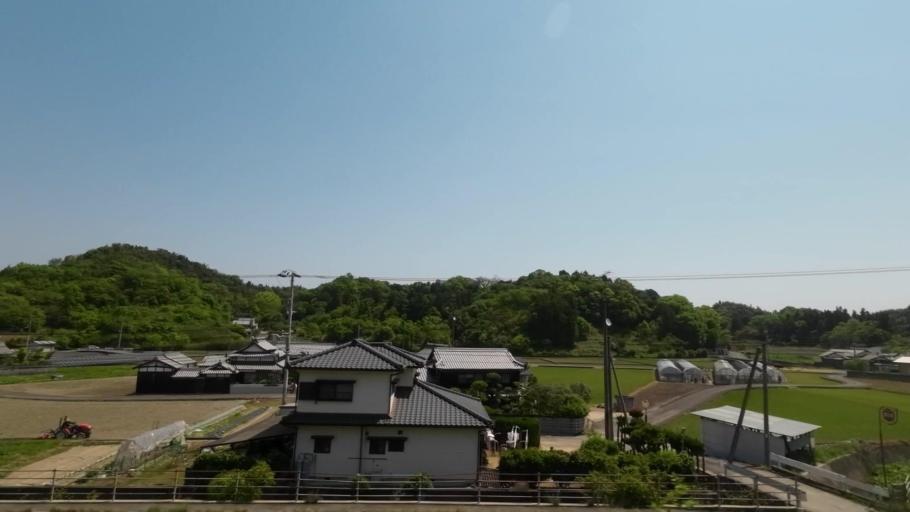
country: JP
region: Ehime
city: Saijo
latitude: 33.9906
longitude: 133.0518
